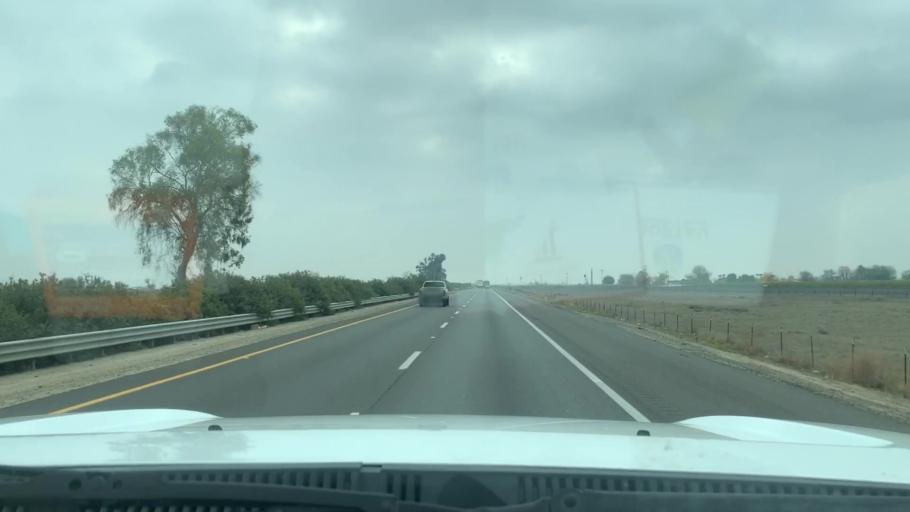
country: US
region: California
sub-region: Tulare County
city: Tipton
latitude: 36.0995
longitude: -119.3228
